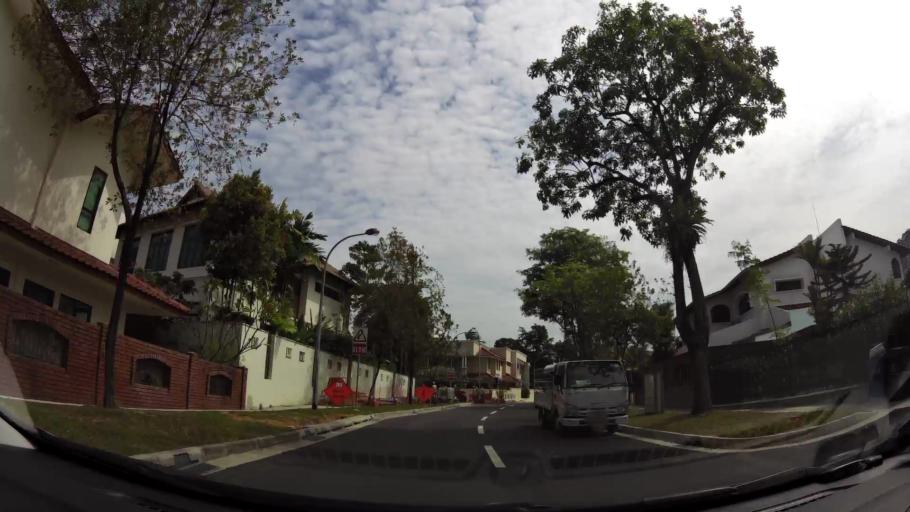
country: SG
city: Singapore
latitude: 1.3209
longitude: 103.7574
